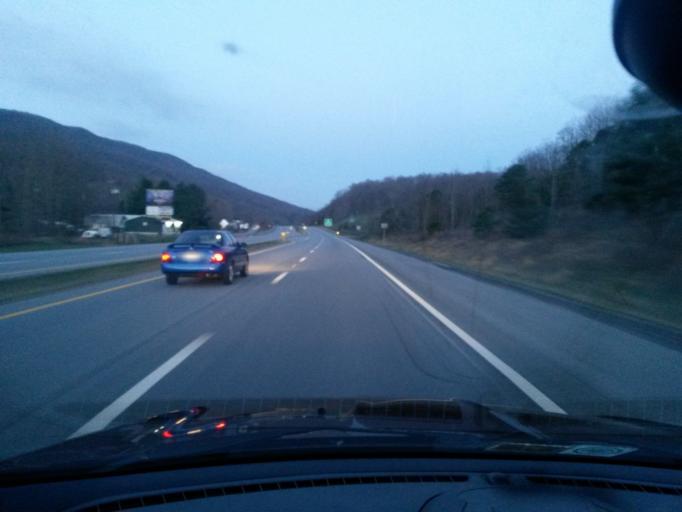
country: US
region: West Virginia
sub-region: Mercer County
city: Bluefield
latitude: 37.2816
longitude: -81.1349
